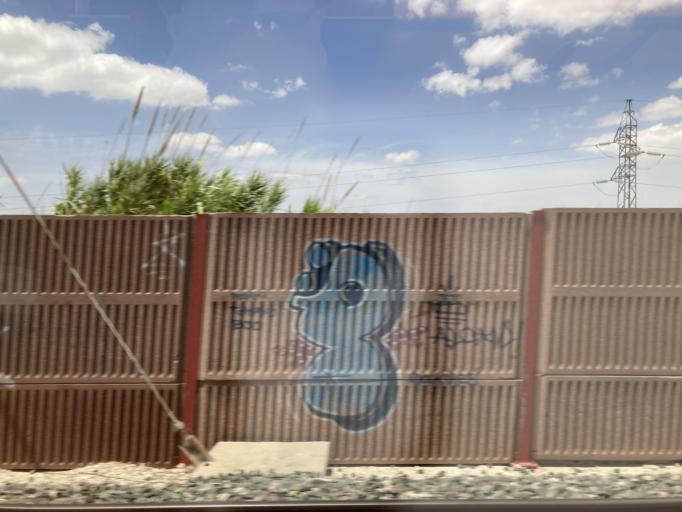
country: ES
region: Andalusia
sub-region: Provincia de Cadiz
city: Jerez de la Frontera
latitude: 36.6676
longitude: -6.1244
